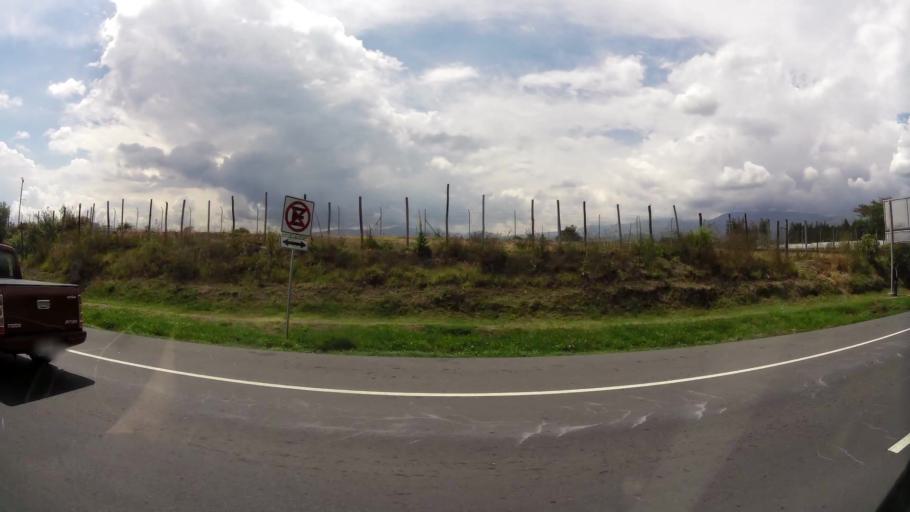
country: EC
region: Pichincha
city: Quito
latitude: -0.1549
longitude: -78.3494
